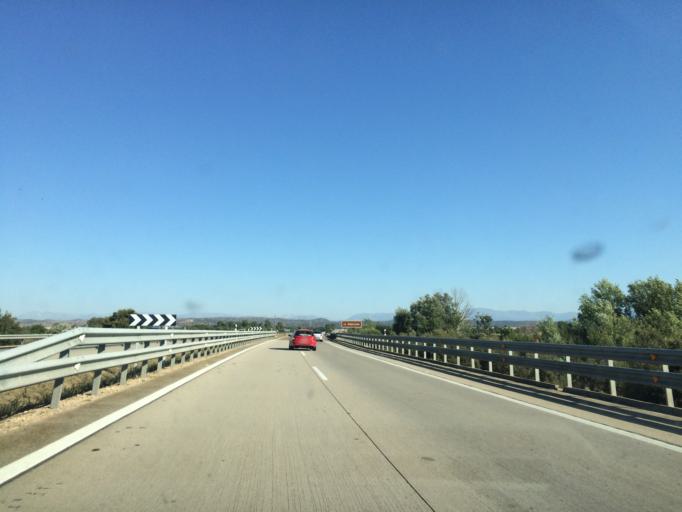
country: ES
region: Castille-La Mancha
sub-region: Province of Toledo
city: Talavera de la Reina
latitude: 39.9847
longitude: -4.7547
